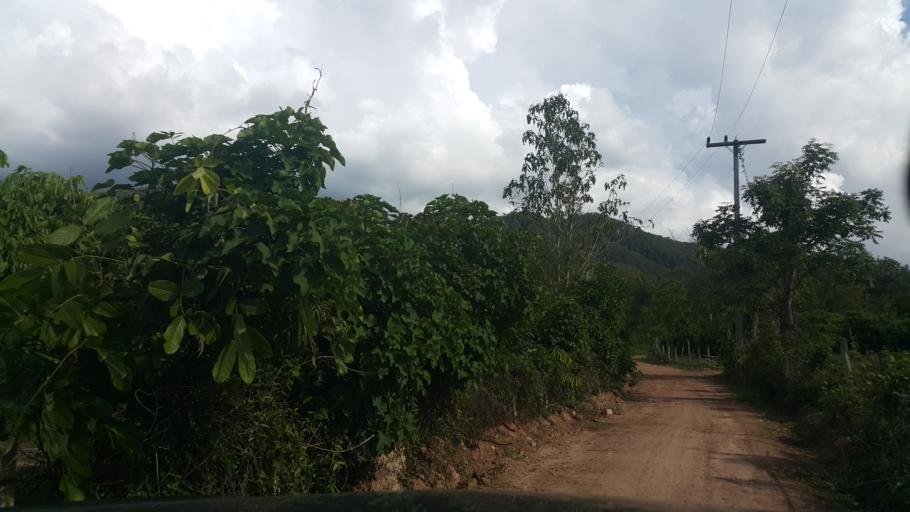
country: TH
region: Chiang Mai
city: Mae On
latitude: 18.7156
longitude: 99.2157
